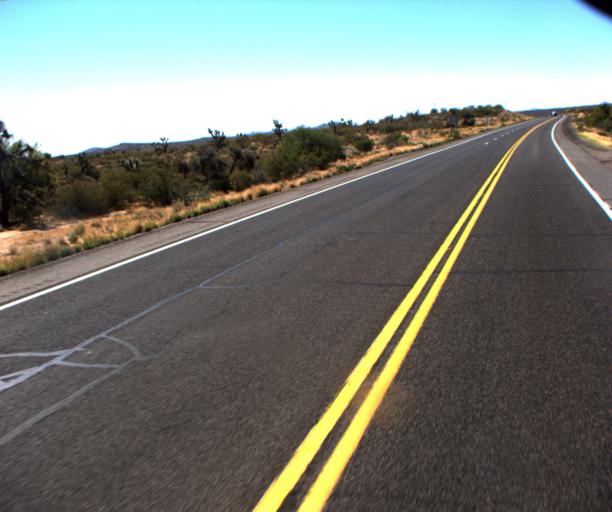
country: US
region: Arizona
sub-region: Yavapai County
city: Congress
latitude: 34.2270
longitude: -113.0697
